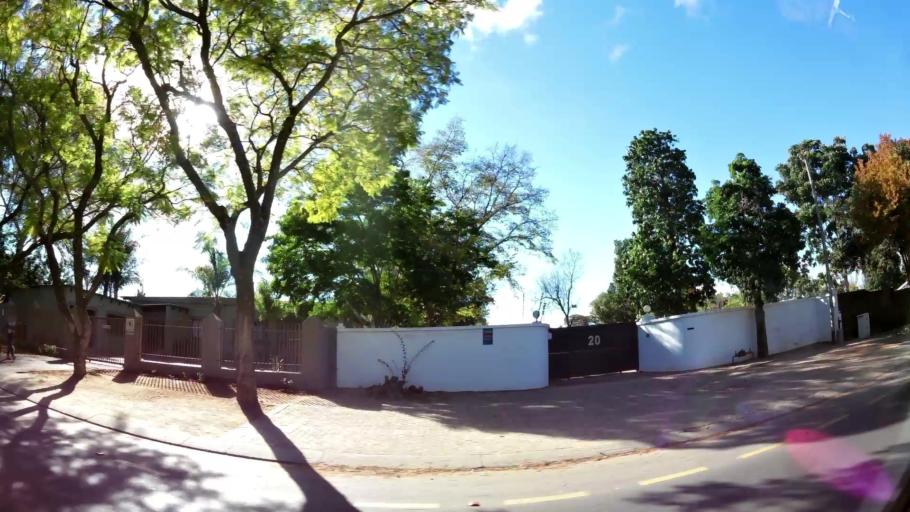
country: ZA
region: Limpopo
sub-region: Capricorn District Municipality
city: Polokwane
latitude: -23.9154
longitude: 29.4614
